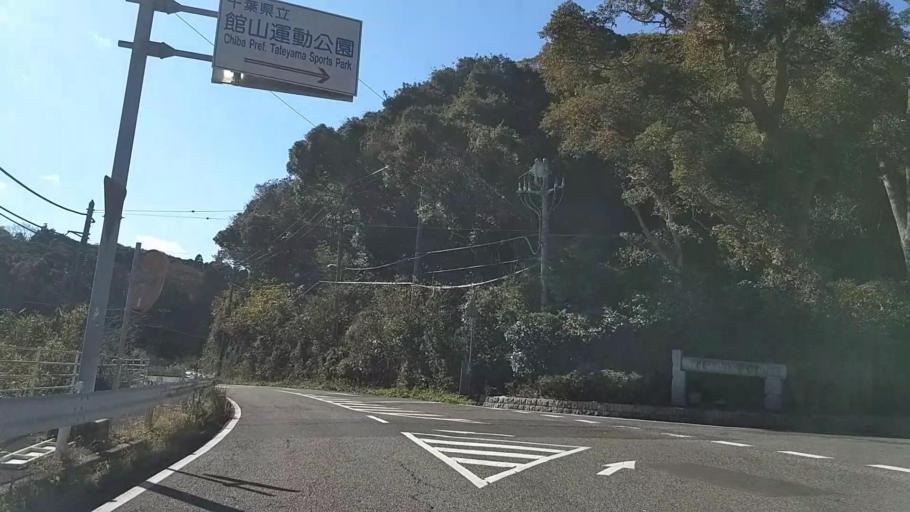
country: JP
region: Chiba
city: Tateyama
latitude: 34.9586
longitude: 139.8515
